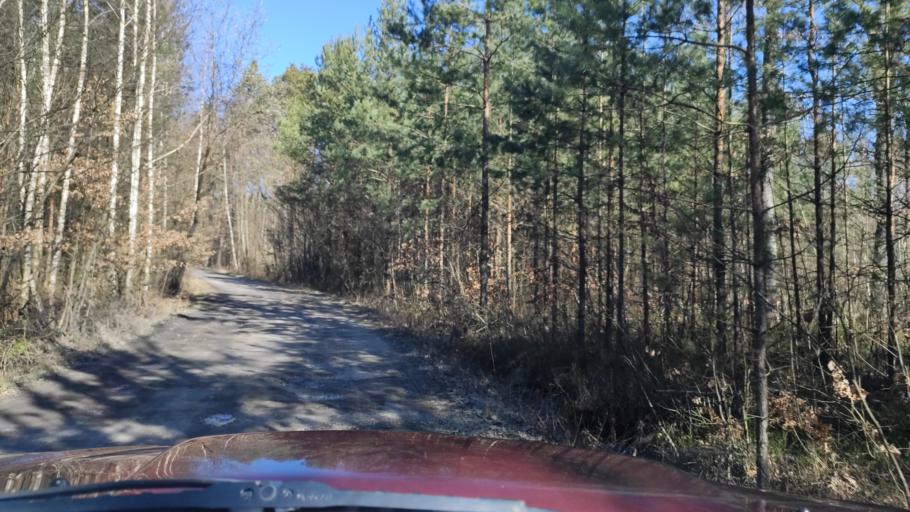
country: PL
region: Masovian Voivodeship
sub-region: Powiat kozienicki
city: Garbatka-Letnisko
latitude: 51.4425
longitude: 21.5363
